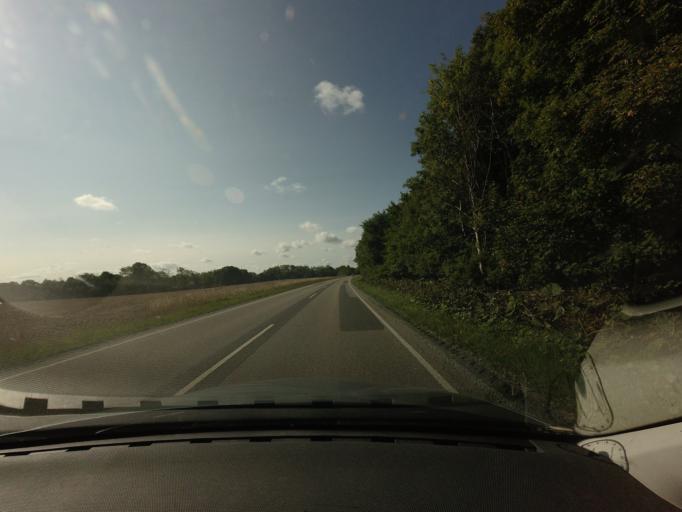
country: DK
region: Zealand
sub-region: Vordingborg Kommune
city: Praesto
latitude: 55.0344
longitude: 12.1039
